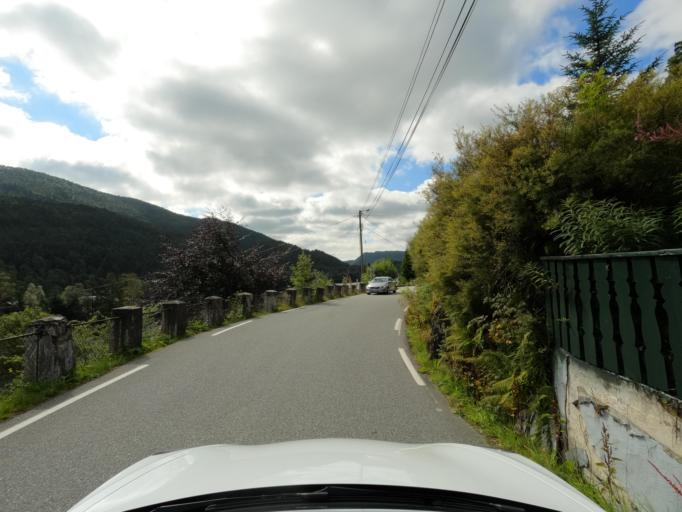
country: NO
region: Hordaland
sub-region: Os
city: Syfteland
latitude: 60.2784
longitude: 5.4588
